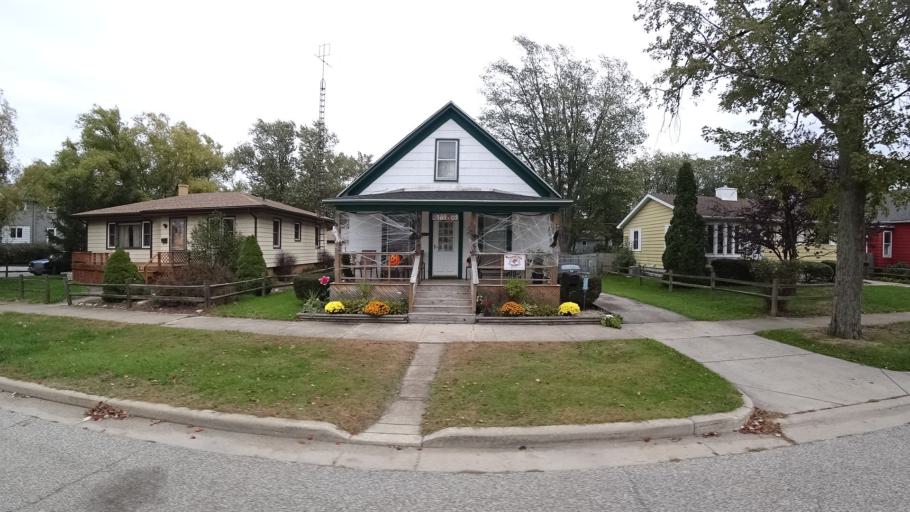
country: US
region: Indiana
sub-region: LaPorte County
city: Michigan City
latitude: 41.7023
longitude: -86.9017
